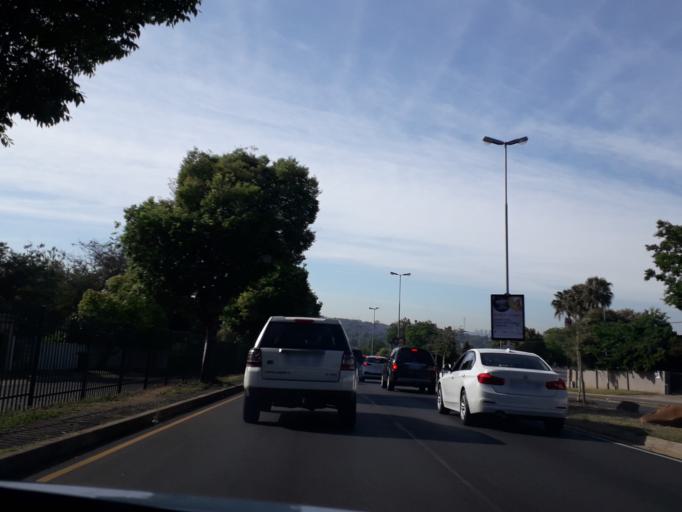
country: ZA
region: Gauteng
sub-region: City of Johannesburg Metropolitan Municipality
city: Johannesburg
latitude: -26.1060
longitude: 28.0154
